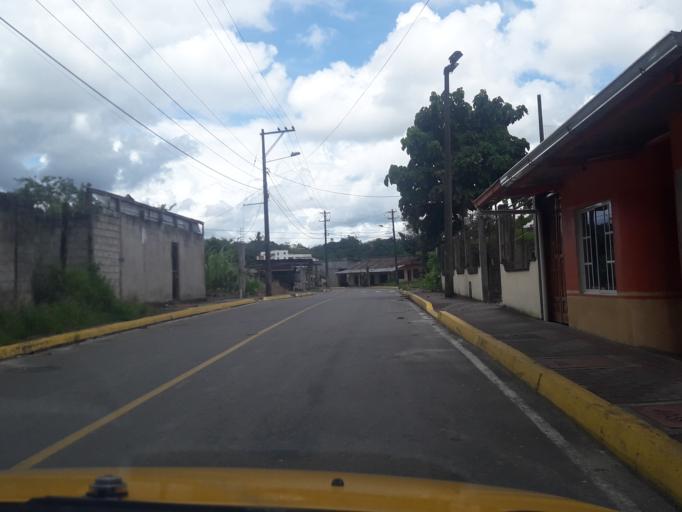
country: EC
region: Napo
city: Tena
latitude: -1.0053
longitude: -77.8188
